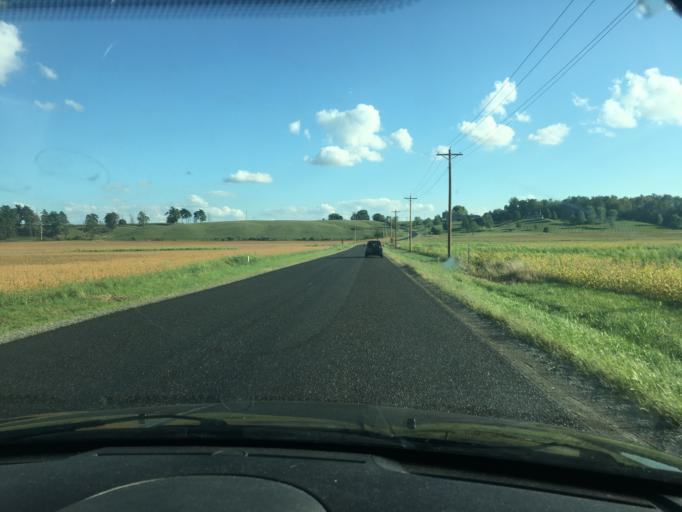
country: US
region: Ohio
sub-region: Logan County
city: West Liberty
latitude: 40.2765
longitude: -83.7242
